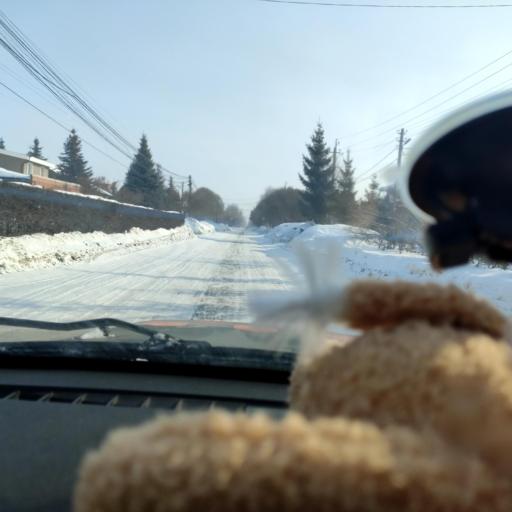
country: RU
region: Samara
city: Podstepki
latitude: 53.5122
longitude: 49.1527
